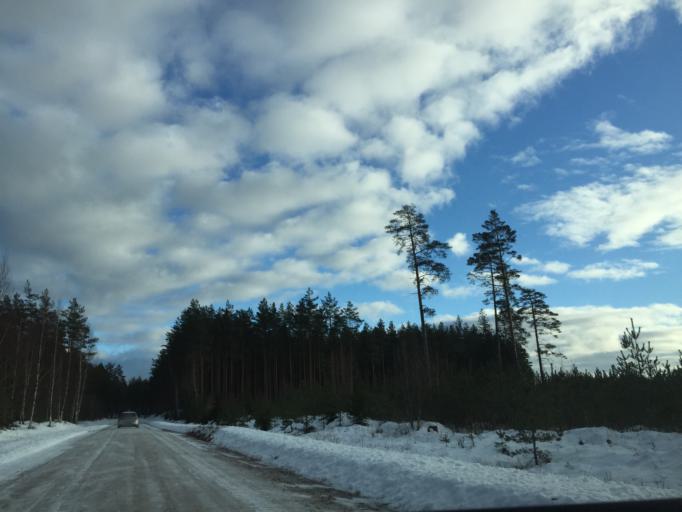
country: LV
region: Lielvarde
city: Lielvarde
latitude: 56.5623
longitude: 24.8373
